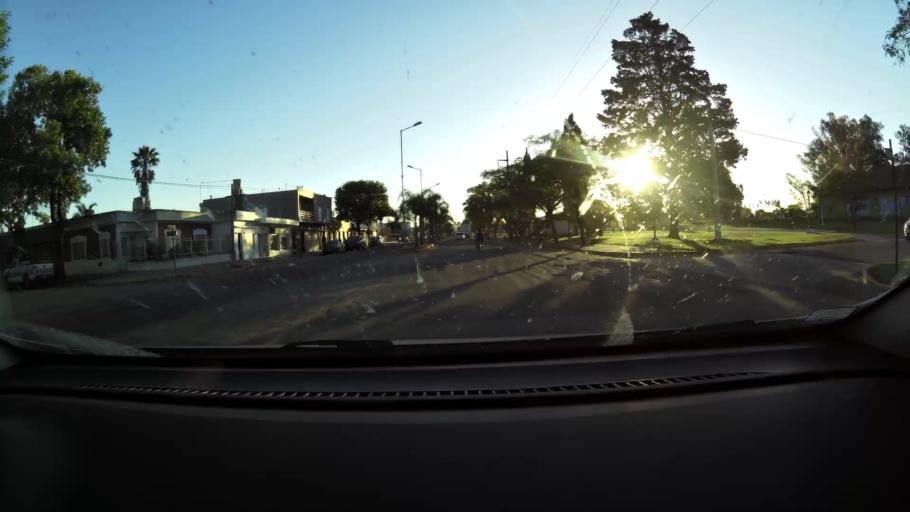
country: AR
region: Cordoba
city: La Playosa
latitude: -32.0992
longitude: -63.0302
